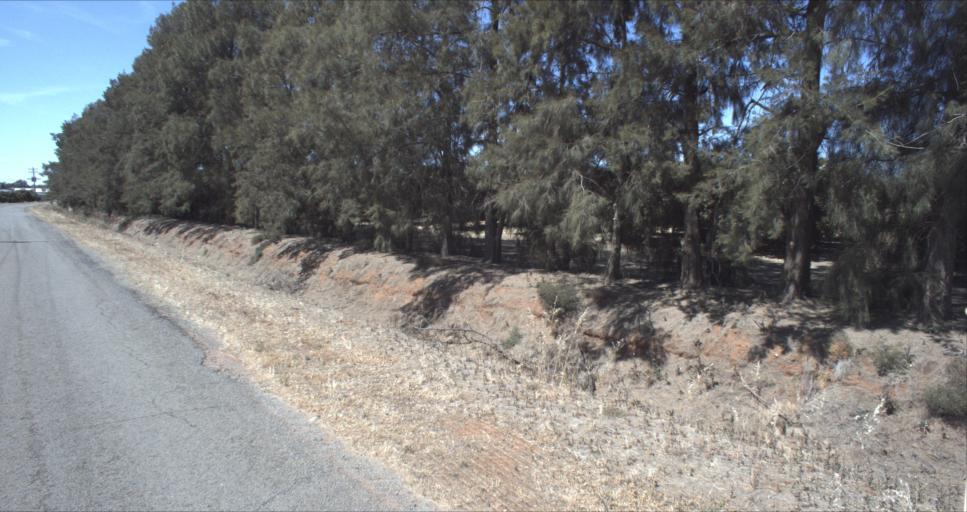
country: AU
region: New South Wales
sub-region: Leeton
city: Leeton
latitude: -34.6016
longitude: 146.4348
